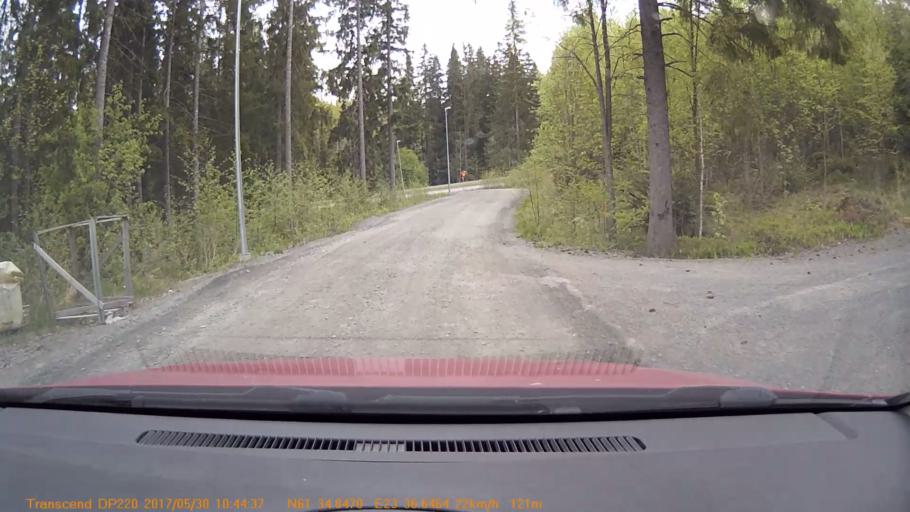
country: FI
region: Pirkanmaa
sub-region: Tampere
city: Yloejaervi
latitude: 61.5809
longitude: 23.6106
